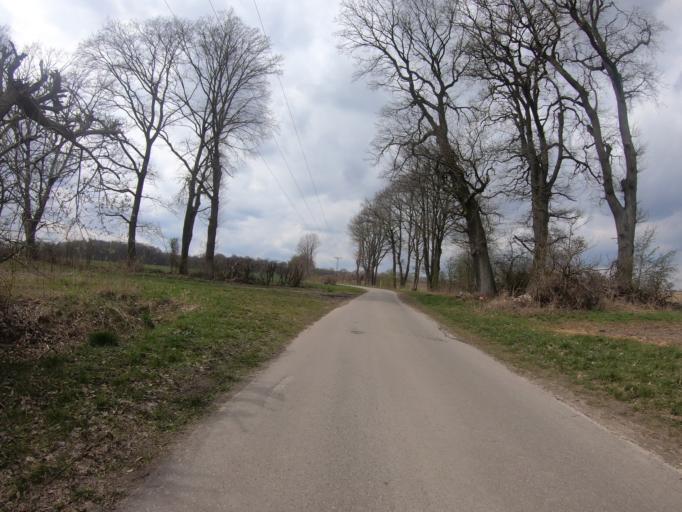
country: DE
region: Lower Saxony
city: Hankensbuttel
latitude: 52.7288
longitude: 10.6348
